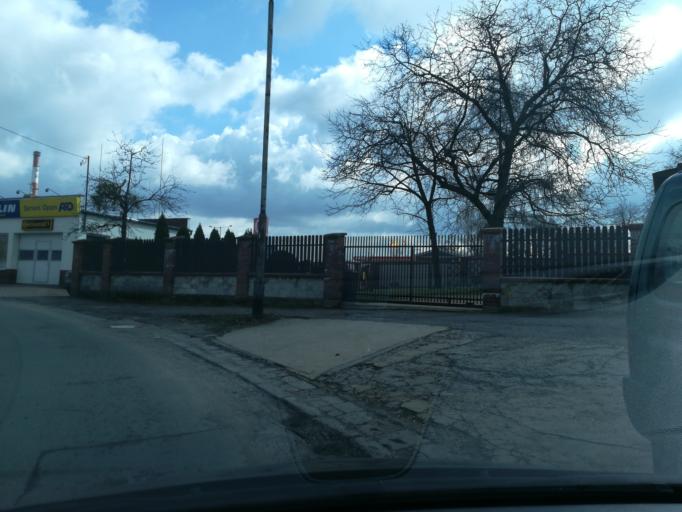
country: PL
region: Silesian Voivodeship
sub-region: Czestochowa
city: Czestochowa
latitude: 50.7941
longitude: 19.1328
